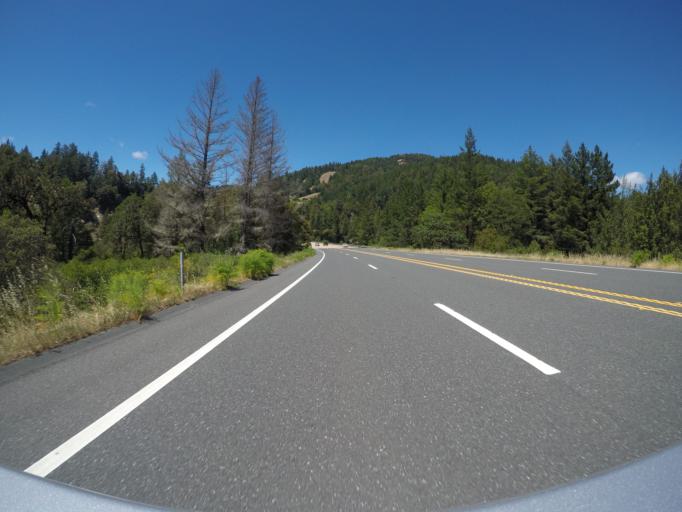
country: US
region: California
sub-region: Humboldt County
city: Redway
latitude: 39.9543
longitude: -123.7800
